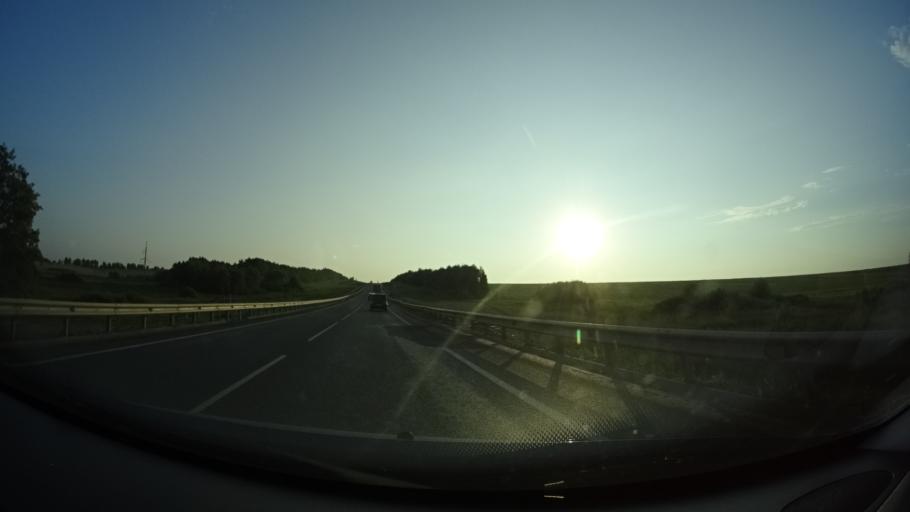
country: RU
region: Samara
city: Kamyshla
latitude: 54.0257
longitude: 51.8787
